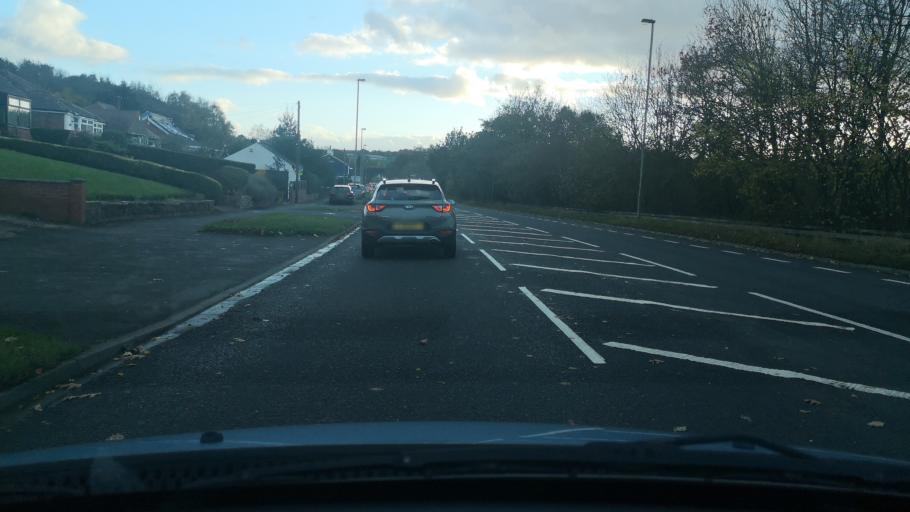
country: GB
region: England
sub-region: City and Borough of Wakefield
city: Crigglestone
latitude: 53.6442
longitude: -1.5463
